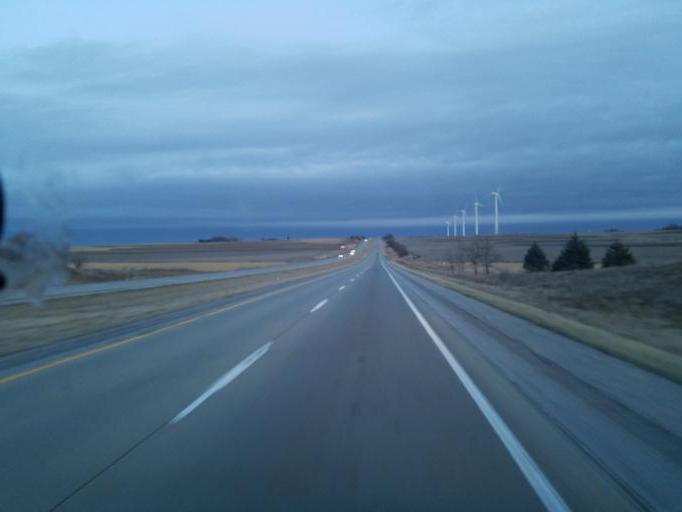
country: US
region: Iowa
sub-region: Pottawattamie County
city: Avoca
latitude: 41.4973
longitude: -95.1951
